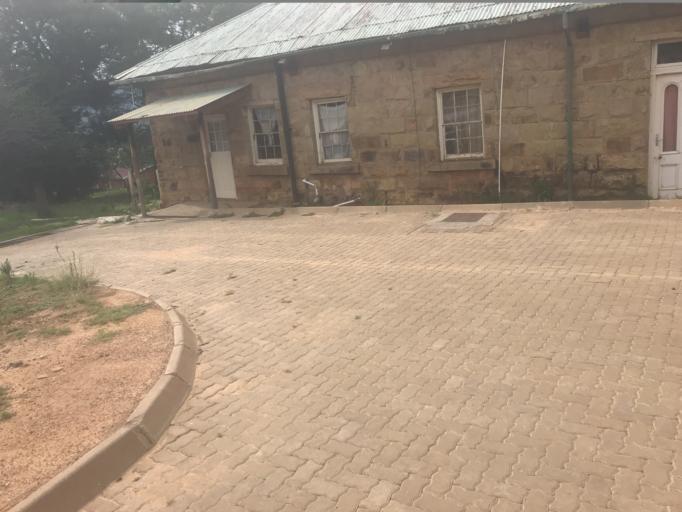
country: LS
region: Maseru
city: Nako
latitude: -29.6302
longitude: 27.5007
